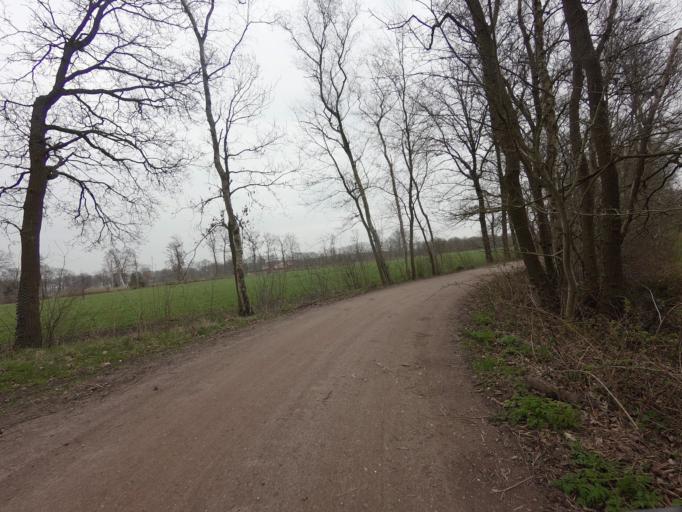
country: NL
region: Utrecht
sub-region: Gemeente Soest
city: Soest
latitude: 52.1683
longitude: 5.2494
